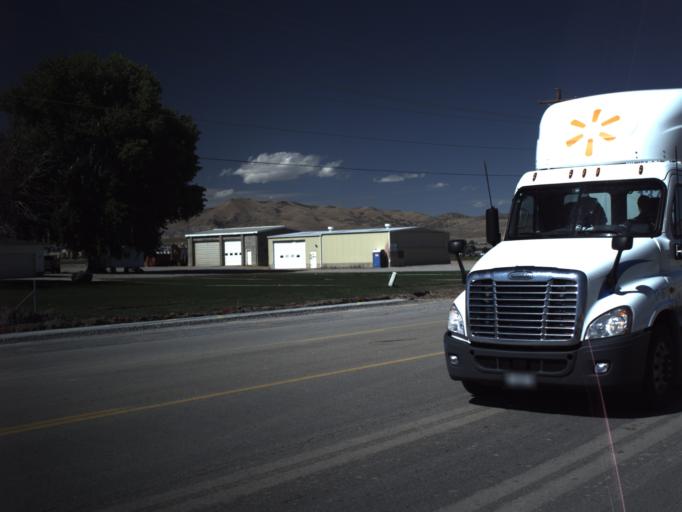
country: US
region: Utah
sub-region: Utah County
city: Saratoga Springs
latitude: 40.3568
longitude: -111.9162
